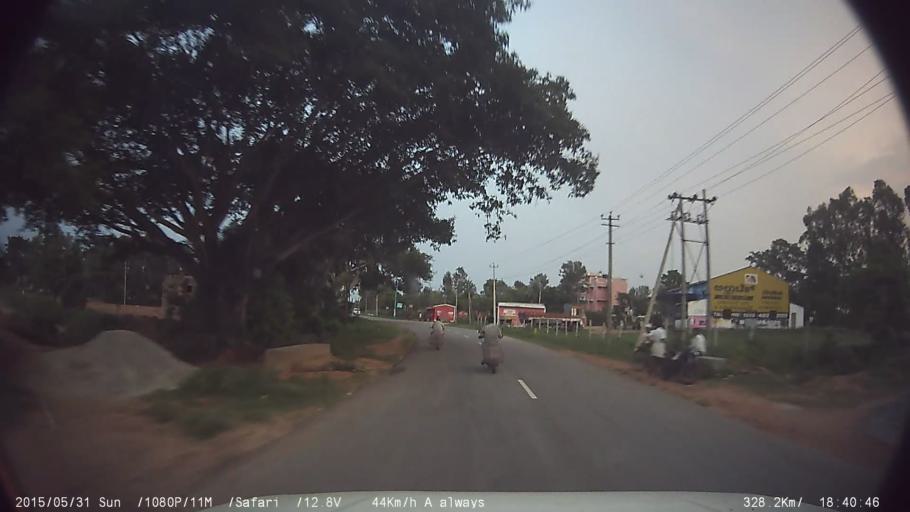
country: IN
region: Karnataka
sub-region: Mysore
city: Nanjangud
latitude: 12.1486
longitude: 76.7882
